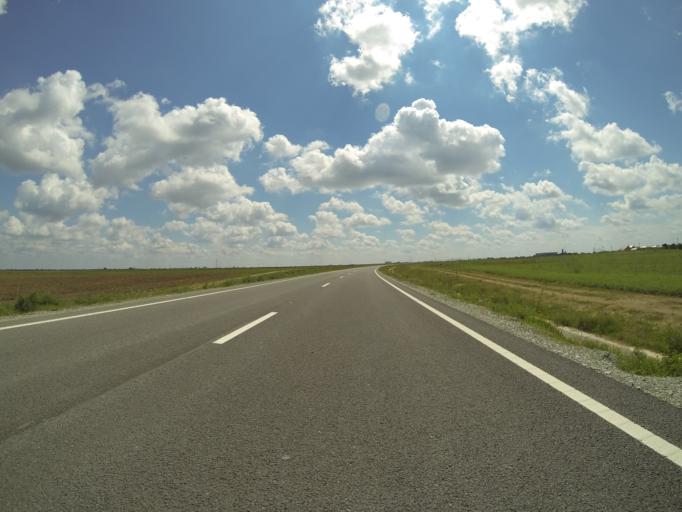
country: RO
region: Dolj
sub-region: Comuna Carcea
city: Carcea
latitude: 44.2678
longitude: 23.9117
